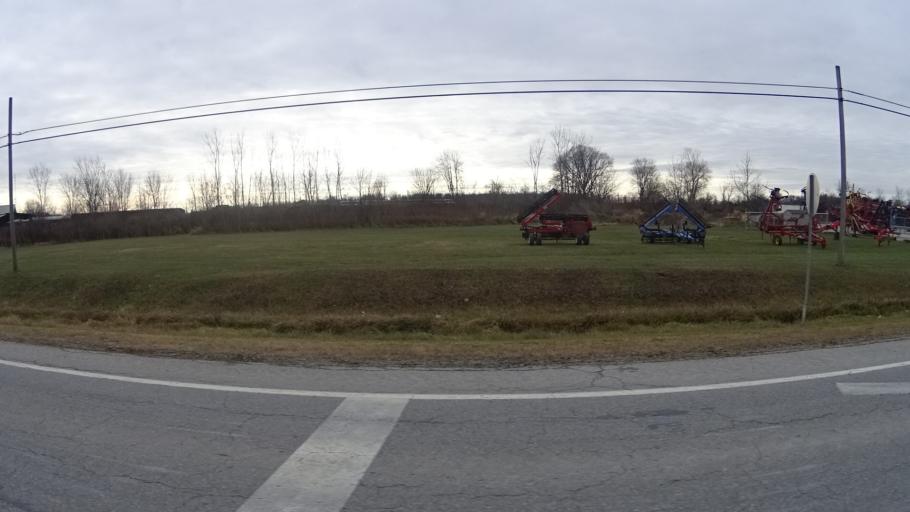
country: US
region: Ohio
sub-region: Lorain County
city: Wellington
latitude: 41.1690
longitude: -82.2368
